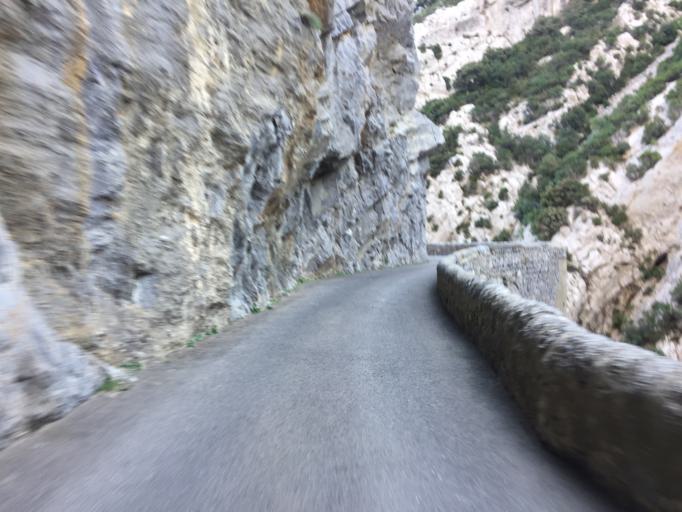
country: FR
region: Languedoc-Roussillon
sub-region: Departement des Pyrenees-Orientales
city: Saint-Paul-de-Fenouillet
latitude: 42.8412
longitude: 2.4796
